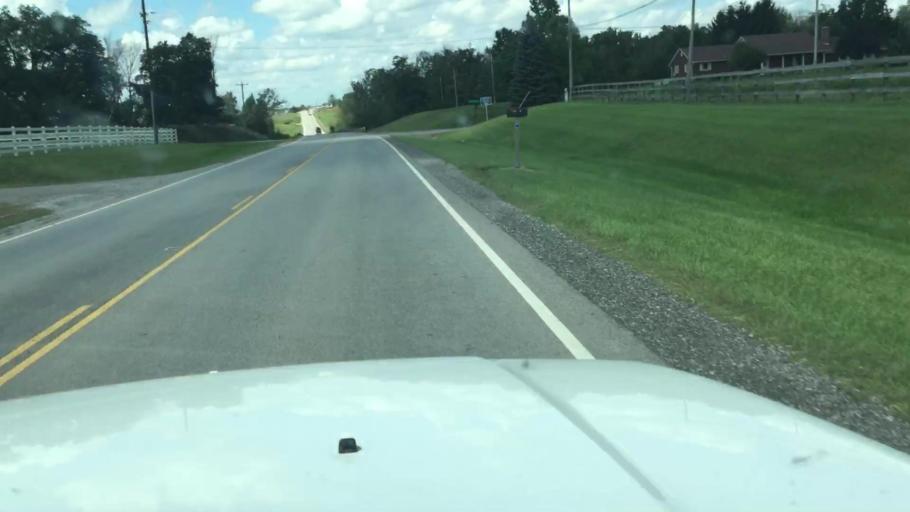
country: US
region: Ohio
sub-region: Madison County
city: Mount Sterling
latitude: 39.7512
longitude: -83.2915
